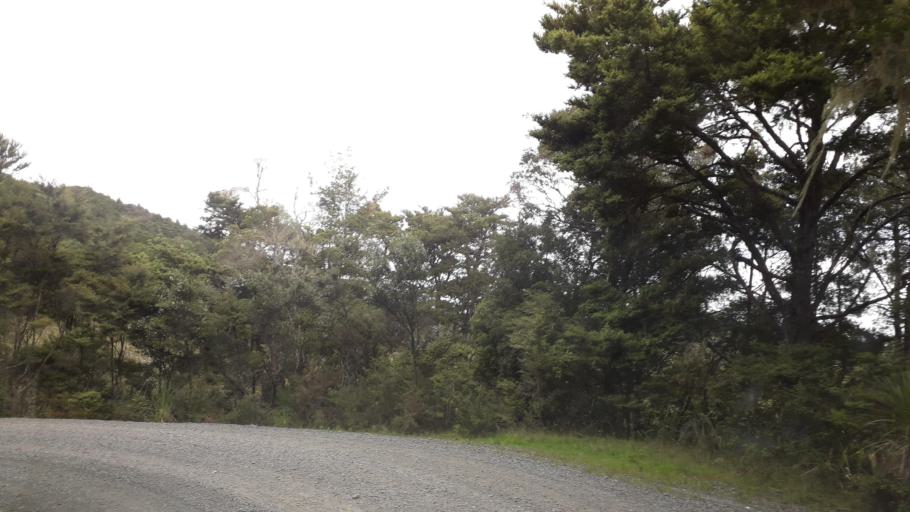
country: NZ
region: Northland
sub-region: Far North District
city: Waimate North
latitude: -35.3062
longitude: 173.5626
